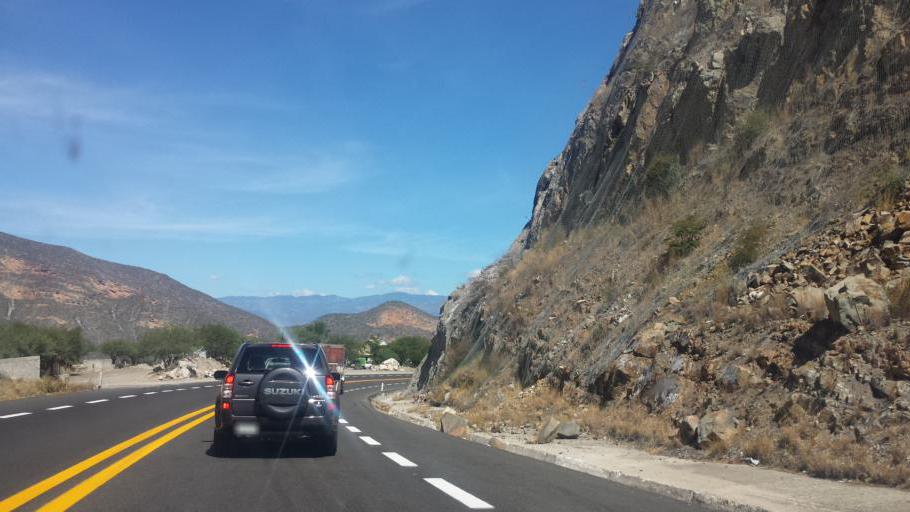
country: MX
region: Puebla
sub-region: San Jose Miahuatlan
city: San Pedro Tetitlan
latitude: 18.1403
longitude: -97.3169
